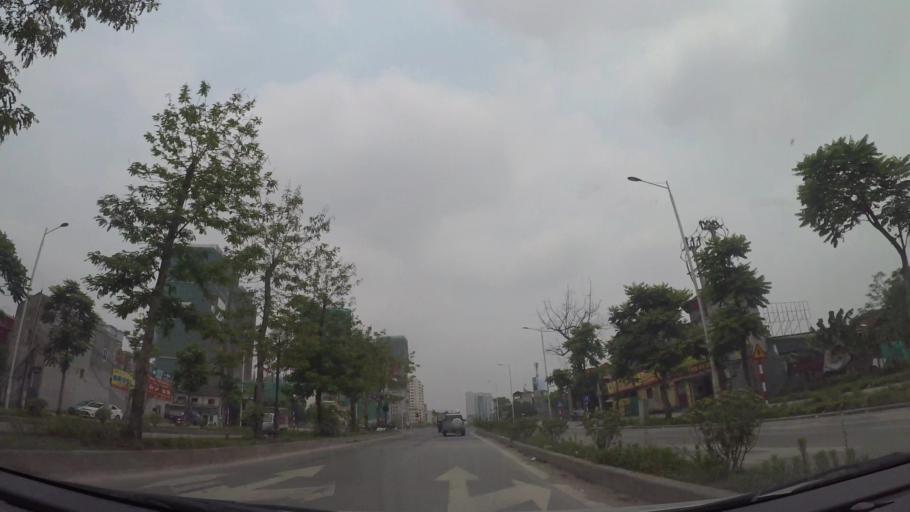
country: VN
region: Ha Noi
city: Cau Dien
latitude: 21.0311
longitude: 105.7577
